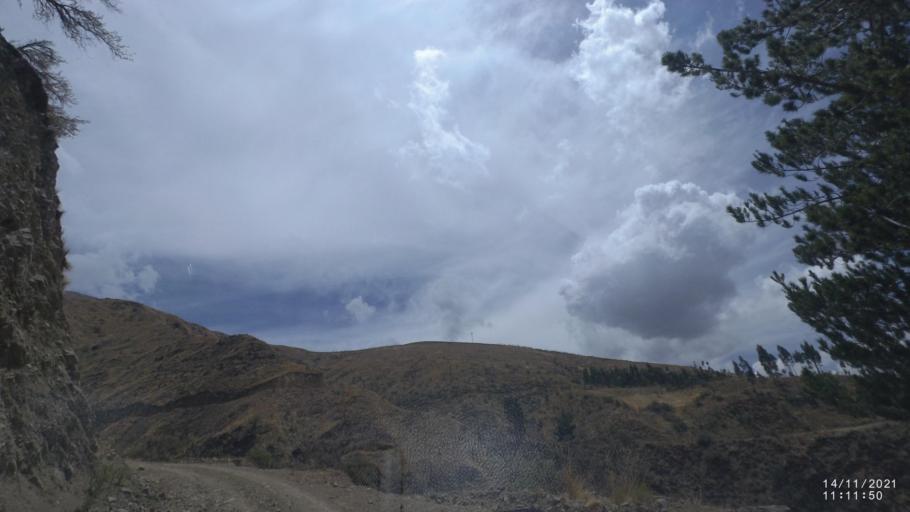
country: BO
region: Cochabamba
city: Cochabamba
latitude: -17.3284
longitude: -66.0509
